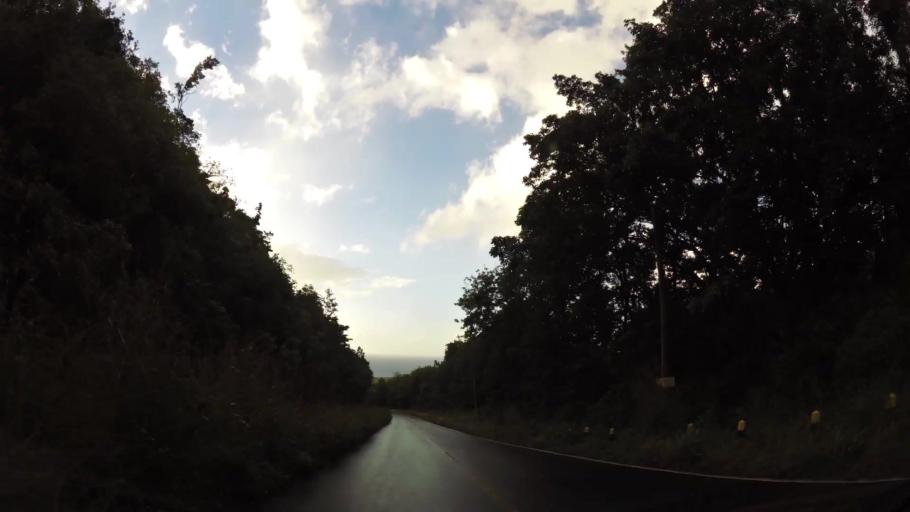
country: DM
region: Saint Peter
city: Colihaut
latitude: 15.5291
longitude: -61.4664
